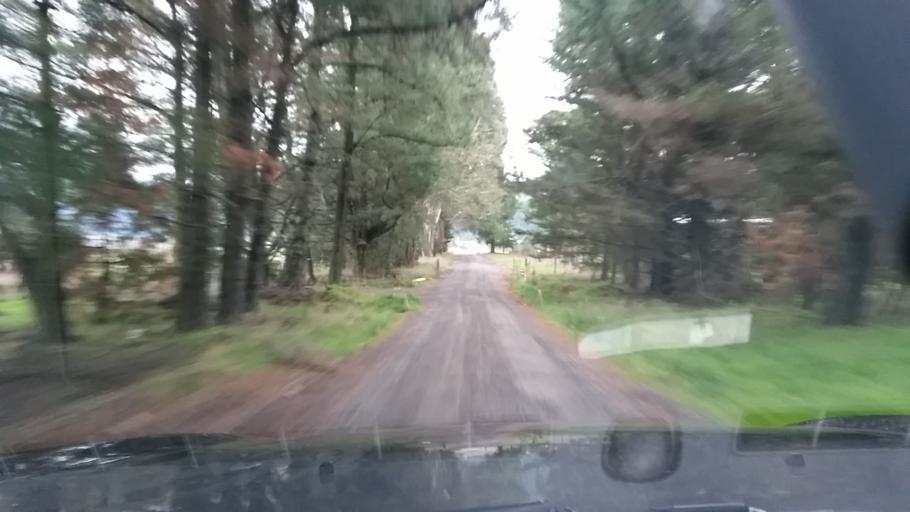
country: NZ
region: Marlborough
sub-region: Marlborough District
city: Blenheim
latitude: -41.5370
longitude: 173.6145
